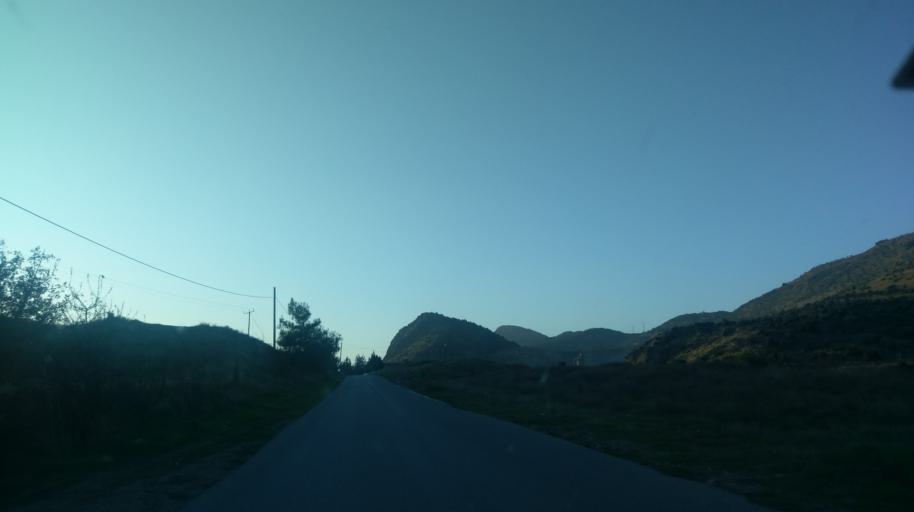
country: CY
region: Lefkosia
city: Nicosia
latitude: 35.2691
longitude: 33.4891
